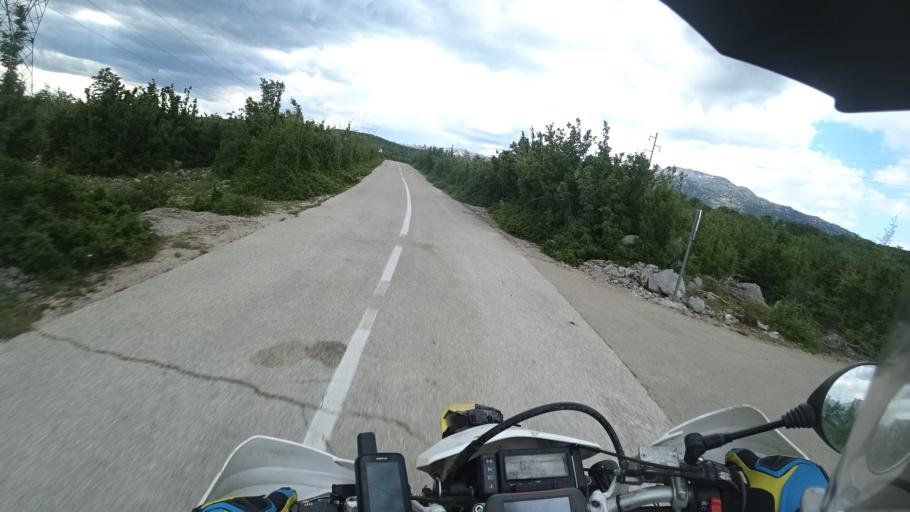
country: HR
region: Zadarska
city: Gracac
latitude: 44.2005
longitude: 15.8649
